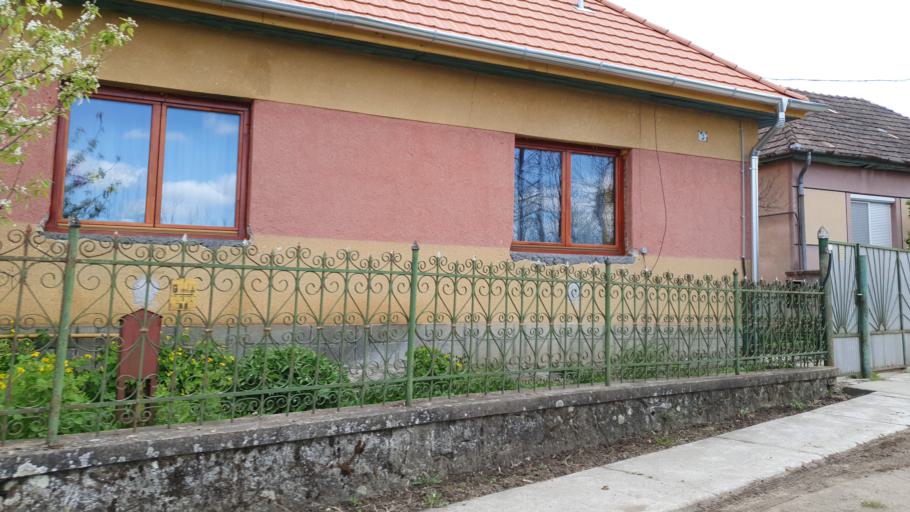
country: HU
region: Pest
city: Acsa
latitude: 47.7895
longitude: 19.3902
